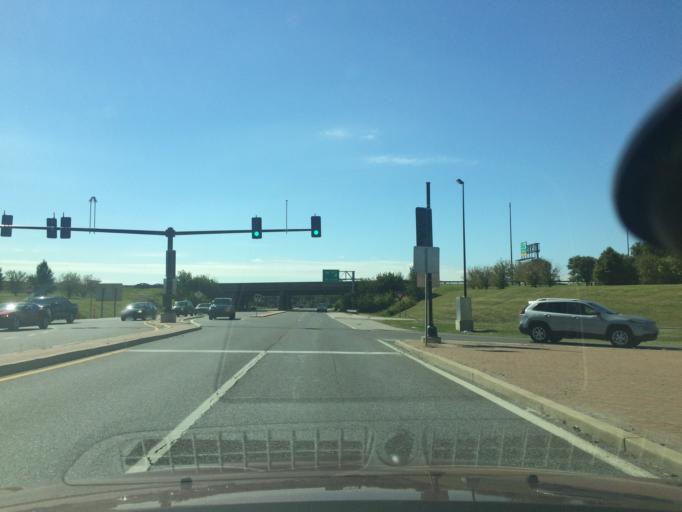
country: US
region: Missouri
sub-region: Saint Charles County
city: Saint Charles
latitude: 38.7701
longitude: -90.4936
